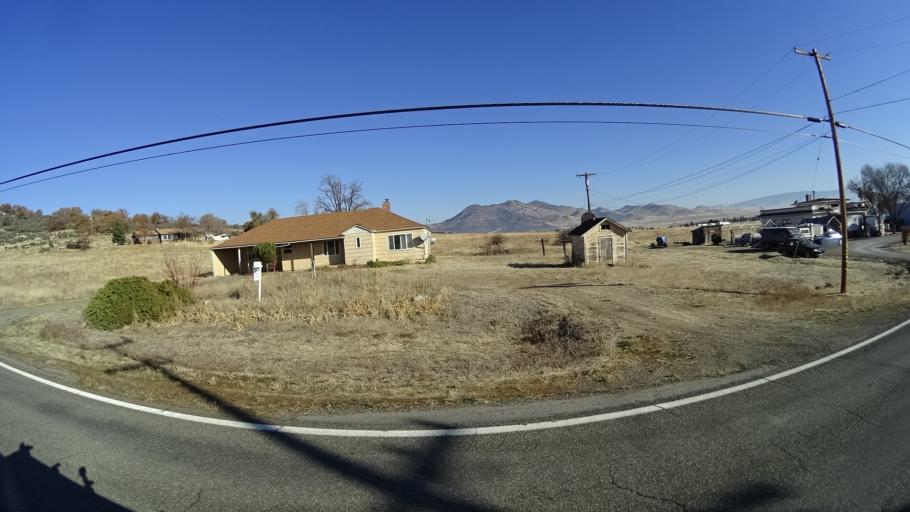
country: US
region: California
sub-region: Siskiyou County
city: Yreka
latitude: 41.7372
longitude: -122.6012
